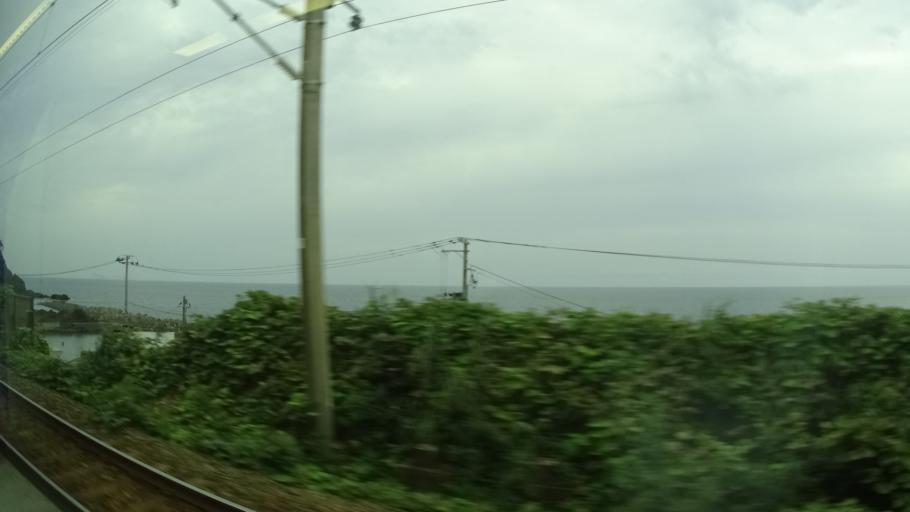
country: JP
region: Yamagata
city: Tsuruoka
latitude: 38.6500
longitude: 139.5995
